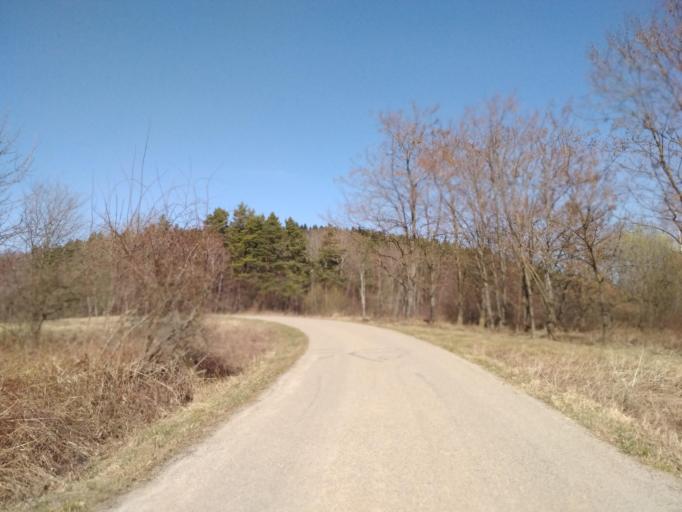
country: PL
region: Subcarpathian Voivodeship
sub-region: Powiat brzozowski
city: Jablonica Polska
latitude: 49.7455
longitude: 21.8935
